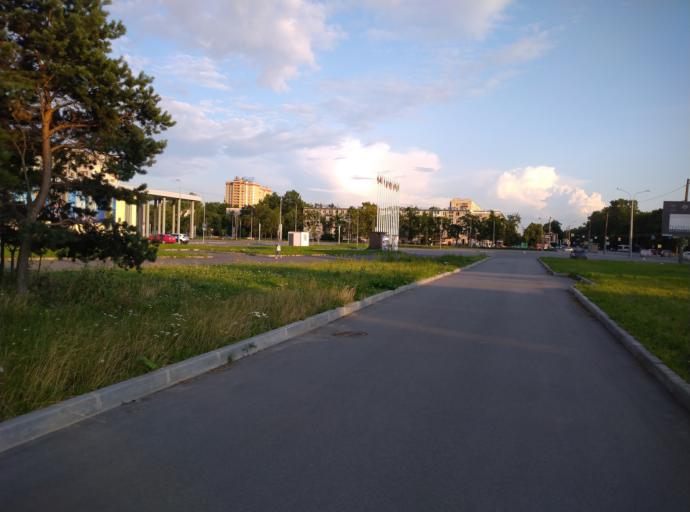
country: RU
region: St.-Petersburg
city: Kupchino
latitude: 59.8662
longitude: 30.3374
